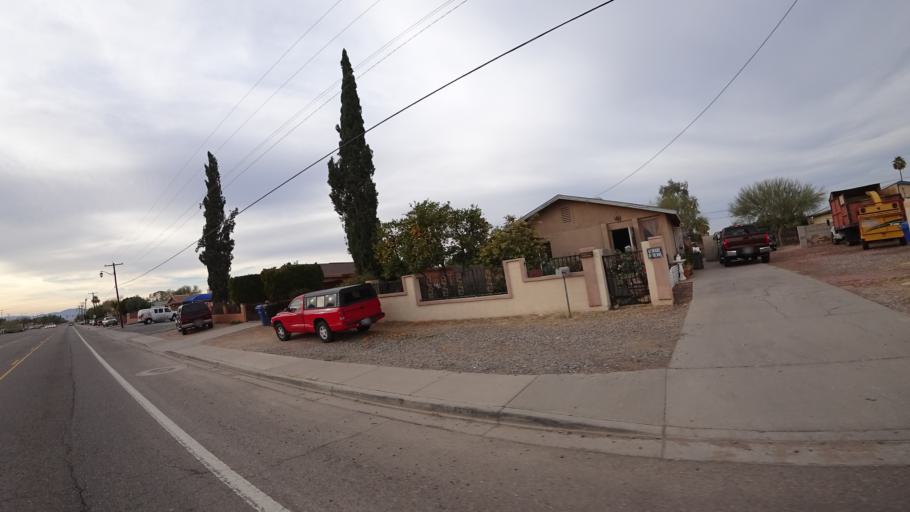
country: US
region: Arizona
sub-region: Maricopa County
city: Surprise
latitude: 33.6236
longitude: -112.3383
